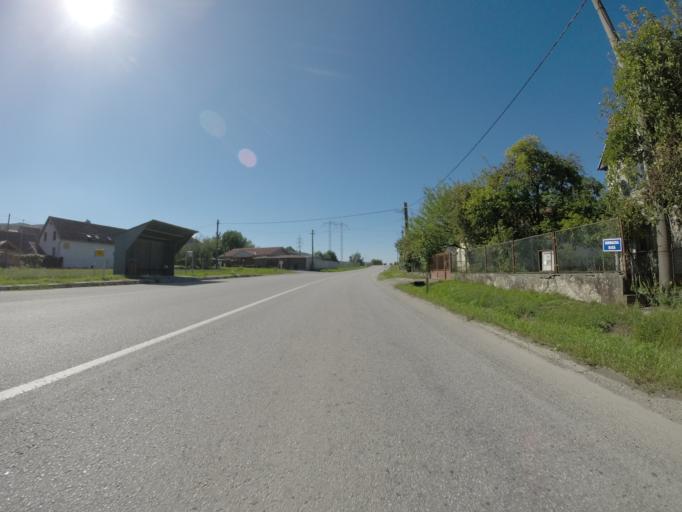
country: SK
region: Nitriansky
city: Ilava
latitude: 49.0172
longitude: 18.2758
